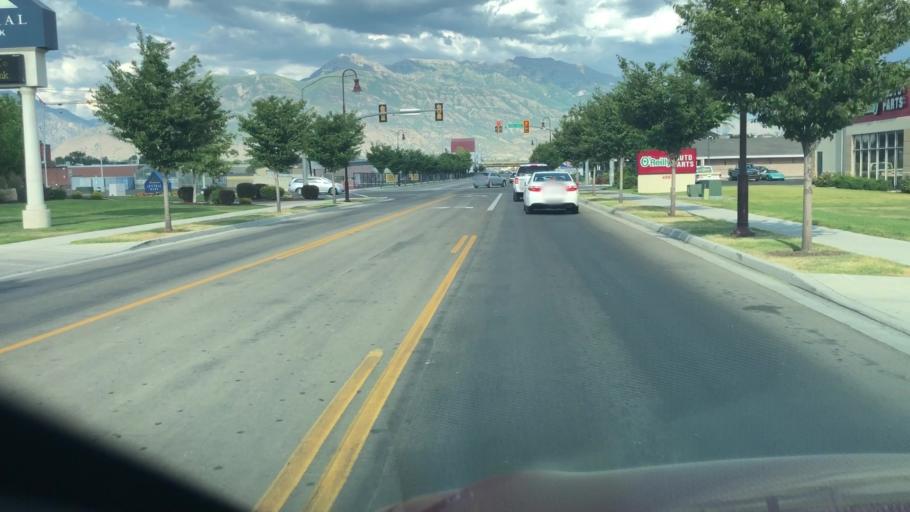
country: US
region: Utah
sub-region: Utah County
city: Lehi
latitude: 40.3880
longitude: -111.8420
